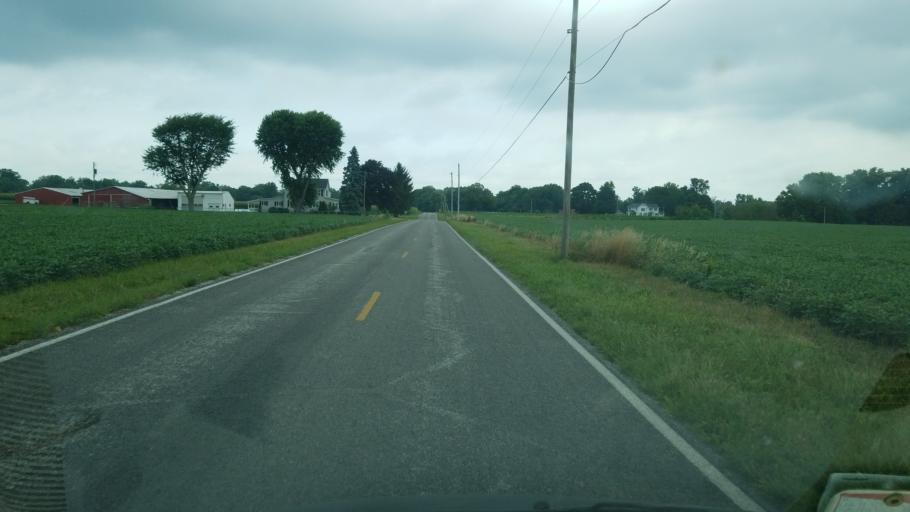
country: US
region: Ohio
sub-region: Sandusky County
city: Green Springs
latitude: 41.2196
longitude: -83.1388
